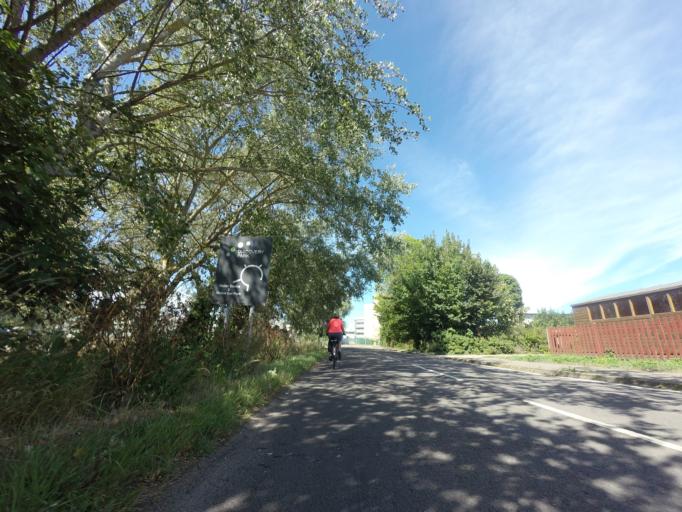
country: GB
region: England
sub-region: Kent
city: Sandwich
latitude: 51.2843
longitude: 1.3454
